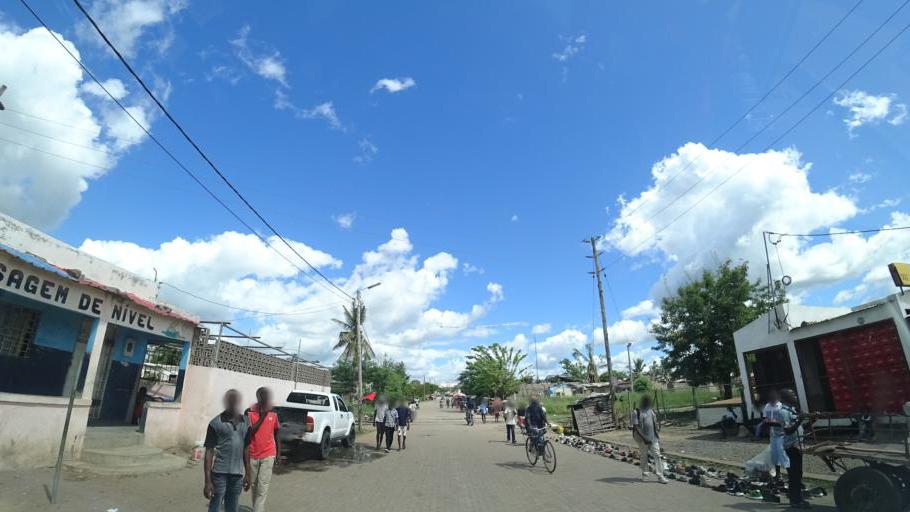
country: MZ
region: Sofala
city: Dondo
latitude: -19.2713
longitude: 34.2074
